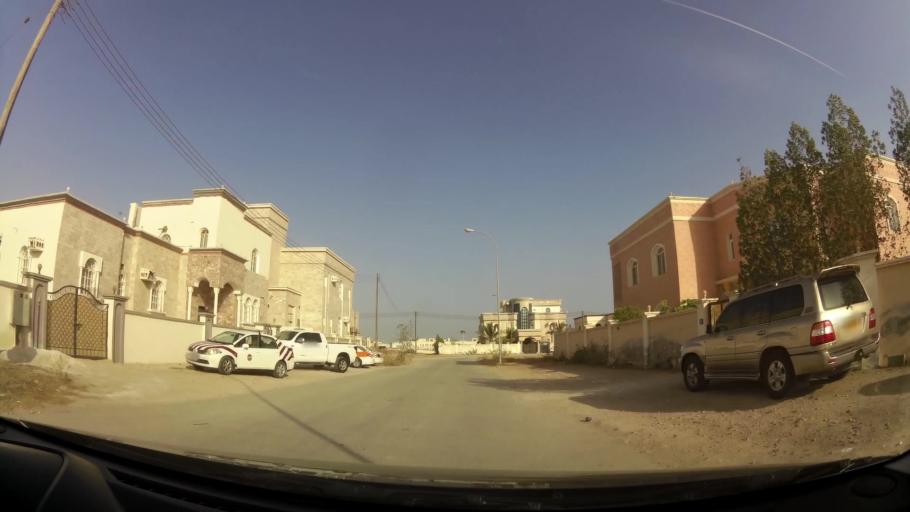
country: OM
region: Zufar
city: Salalah
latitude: 17.0190
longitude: 54.0221
